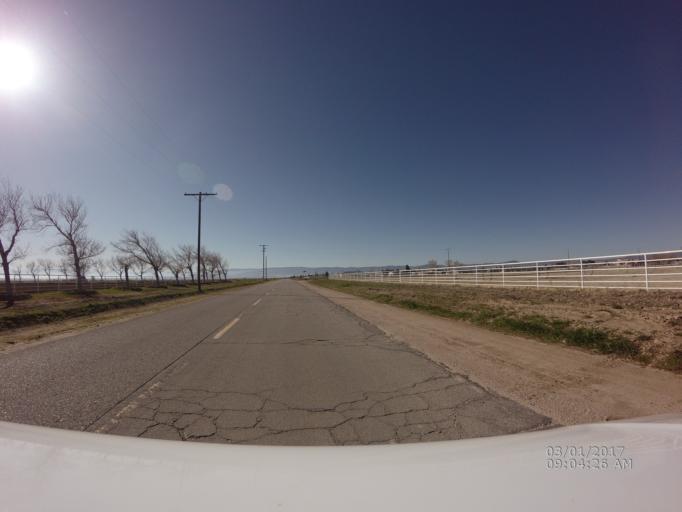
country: US
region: California
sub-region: Los Angeles County
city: Quartz Hill
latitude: 34.7701
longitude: -118.2726
